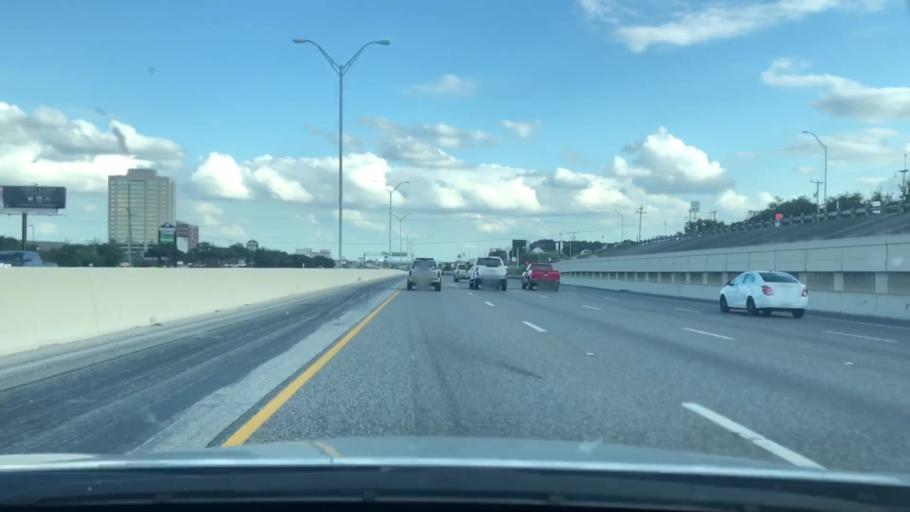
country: US
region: Texas
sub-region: Bexar County
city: Shavano Park
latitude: 29.5379
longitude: -98.5693
